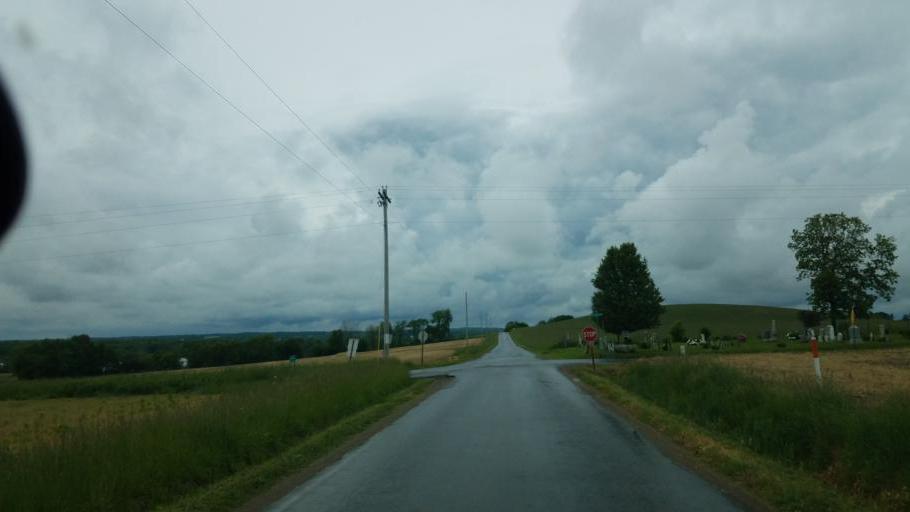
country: US
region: Ohio
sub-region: Richland County
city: Lexington
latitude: 40.6007
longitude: -82.6243
